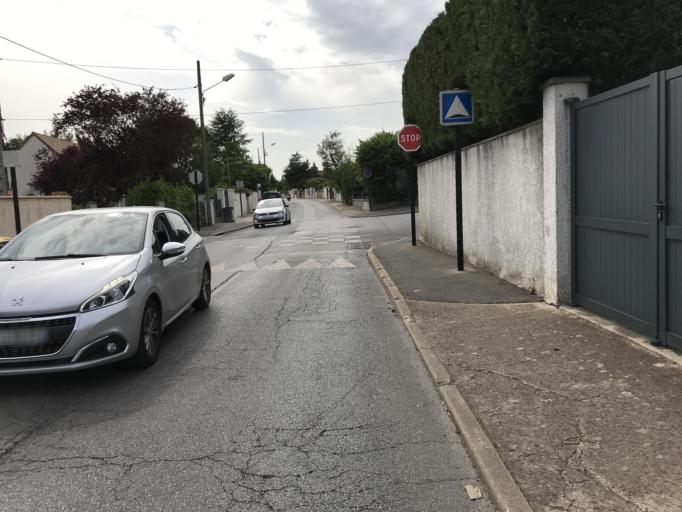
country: FR
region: Ile-de-France
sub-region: Departement de l'Essonne
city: La Ville-du-Bois
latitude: 48.6648
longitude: 2.2685
